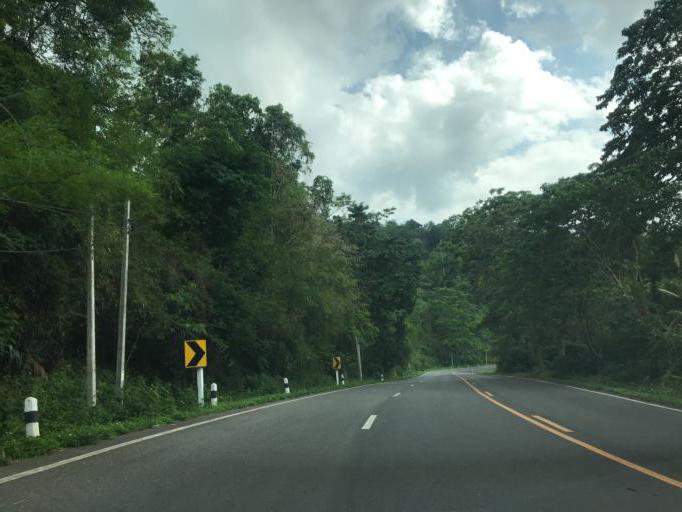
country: TH
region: Phayao
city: Phayao
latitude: 19.0592
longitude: 99.7915
